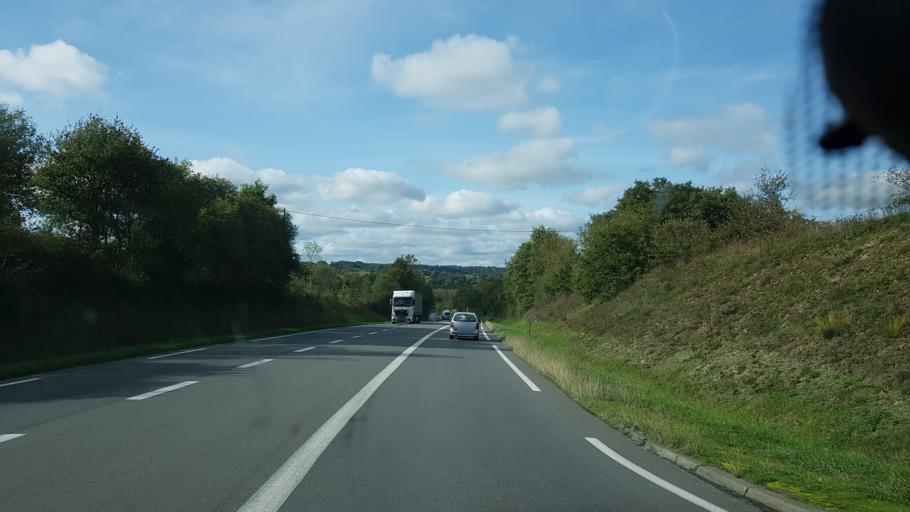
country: FR
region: Poitou-Charentes
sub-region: Departement de la Charente
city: Confolens
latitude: 46.0636
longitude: 0.6912
